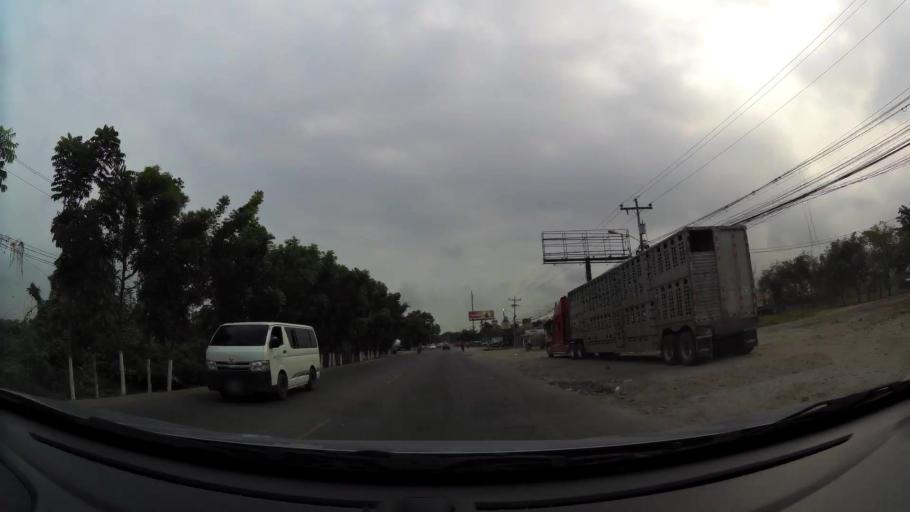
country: HN
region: Yoro
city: El Progreso
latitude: 15.4174
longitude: -87.8014
